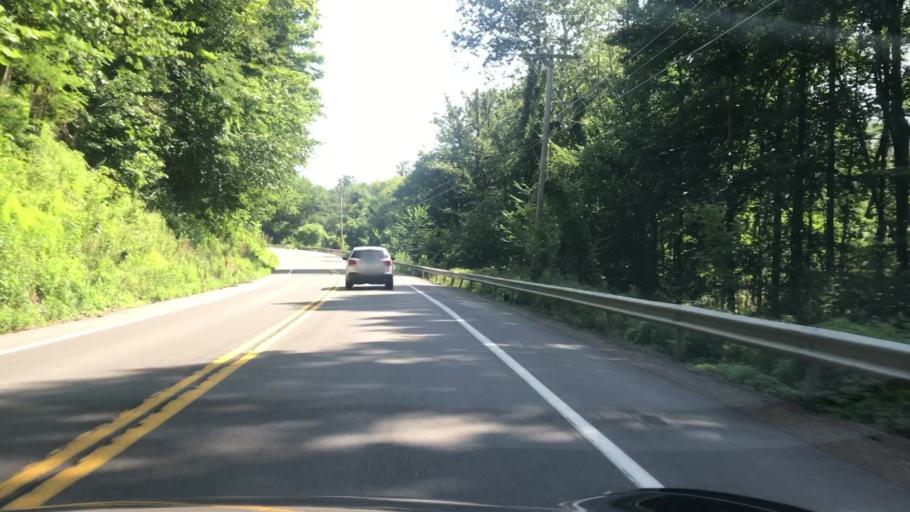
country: US
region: Pennsylvania
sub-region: Lycoming County
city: Garden View
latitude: 41.4255
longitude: -77.0136
